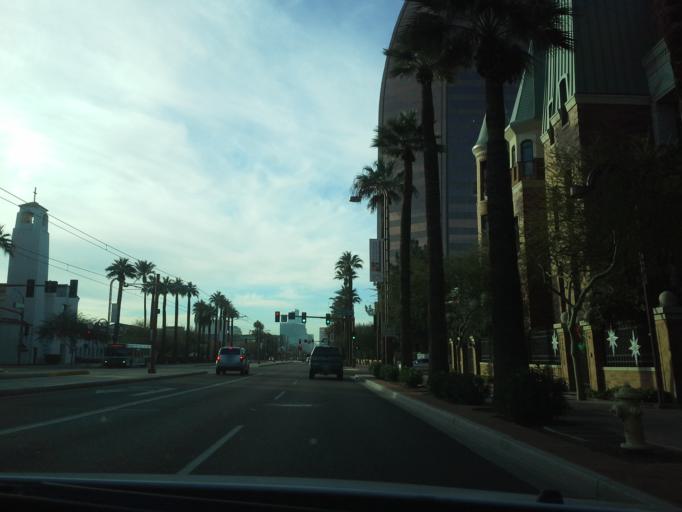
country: US
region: Arizona
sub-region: Maricopa County
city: Phoenix
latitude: 33.4700
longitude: -112.0739
